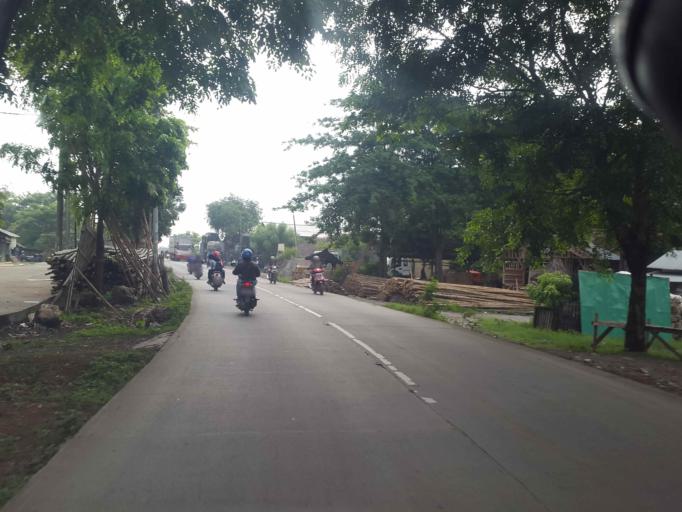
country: ID
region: West Java
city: Cikarang
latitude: -6.2946
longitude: 107.1195
